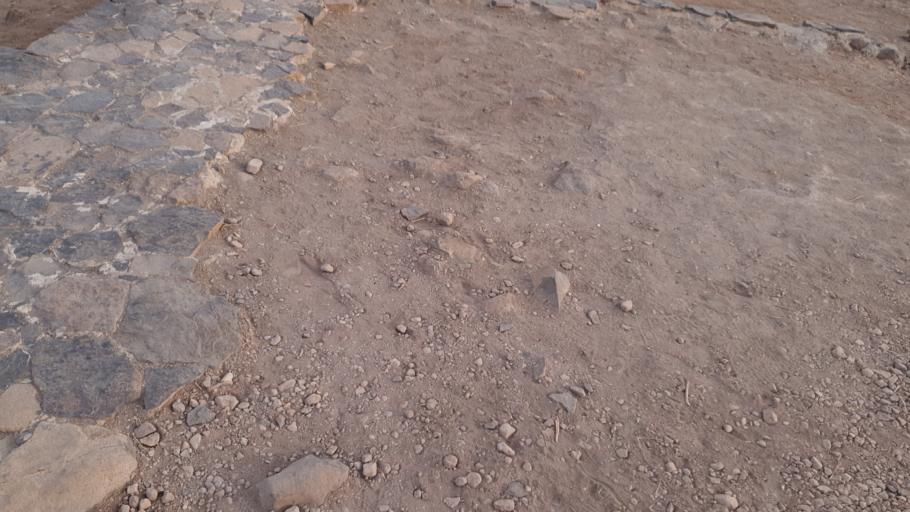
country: ID
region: East Nusa Tenggara
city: Komodo
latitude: -8.6791
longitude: 119.5564
